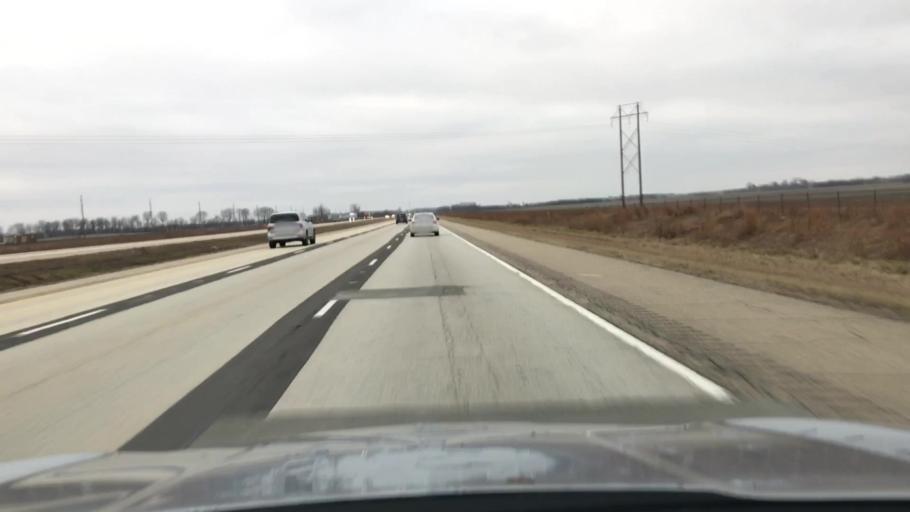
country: US
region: Illinois
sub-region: Sangamon County
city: Williamsville
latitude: 39.9922
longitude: -89.5133
